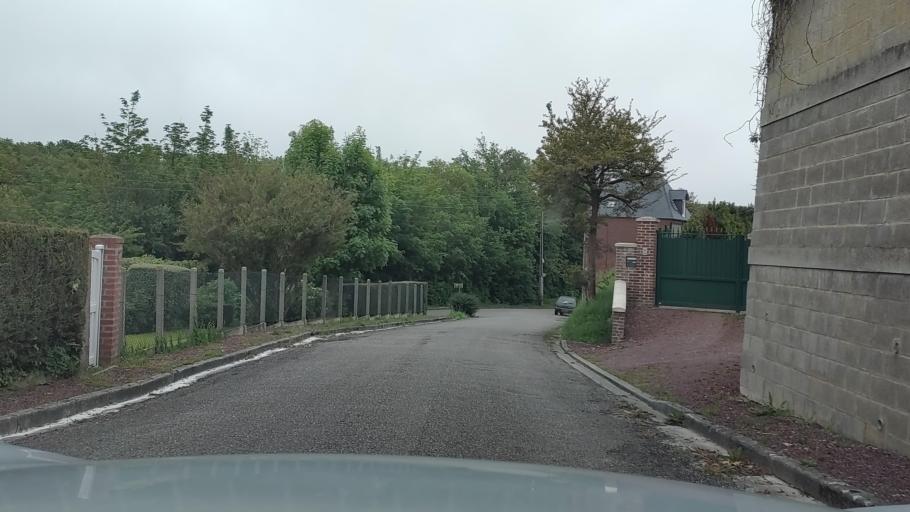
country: FR
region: Picardie
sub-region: Departement de la Somme
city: Ault
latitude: 50.0976
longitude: 1.4475
